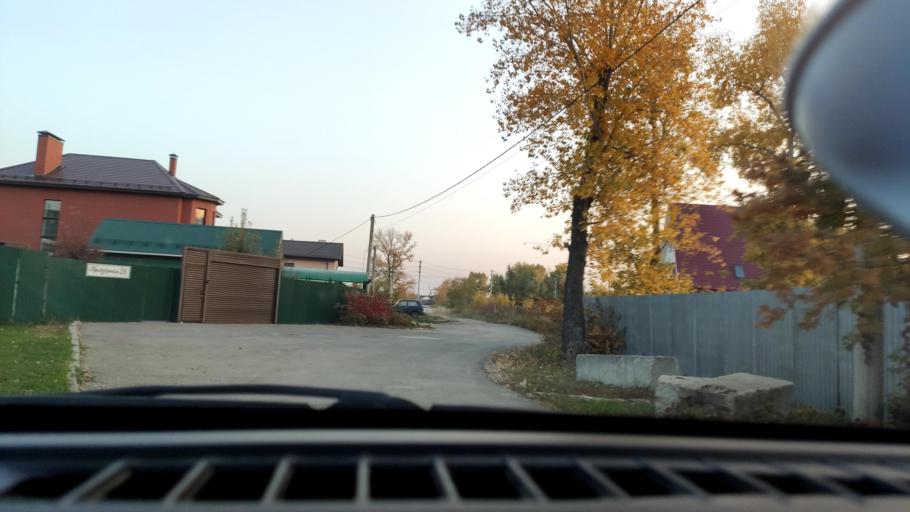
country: RU
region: Samara
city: Samara
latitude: 53.1499
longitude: 50.0861
